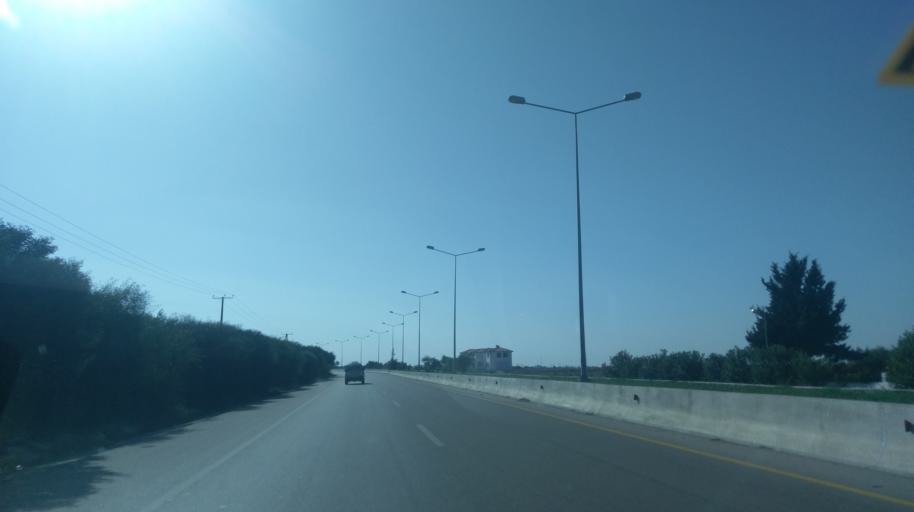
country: CY
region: Ammochostos
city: Trikomo
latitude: 35.2379
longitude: 33.8989
